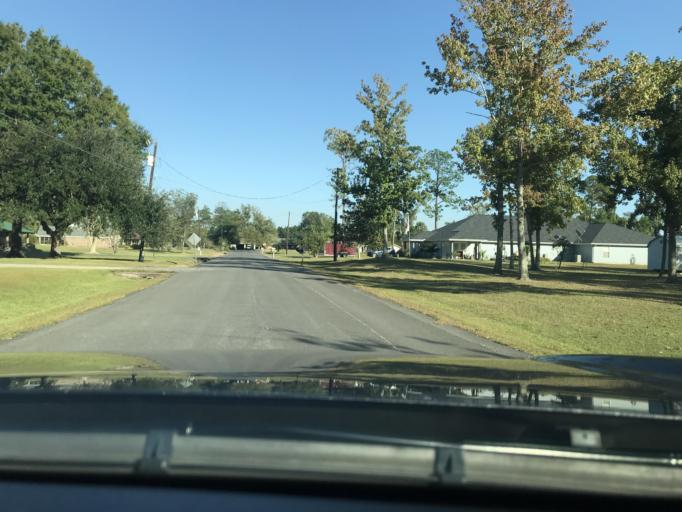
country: US
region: Louisiana
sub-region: Calcasieu Parish
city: Westlake
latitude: 30.3170
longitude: -93.2735
